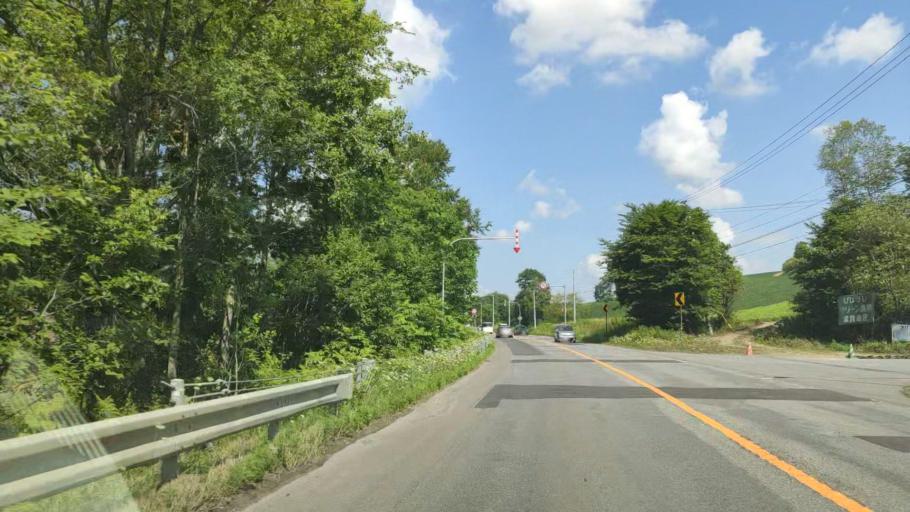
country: JP
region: Hokkaido
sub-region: Asahikawa-shi
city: Asahikawa
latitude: 43.5769
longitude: 142.4394
